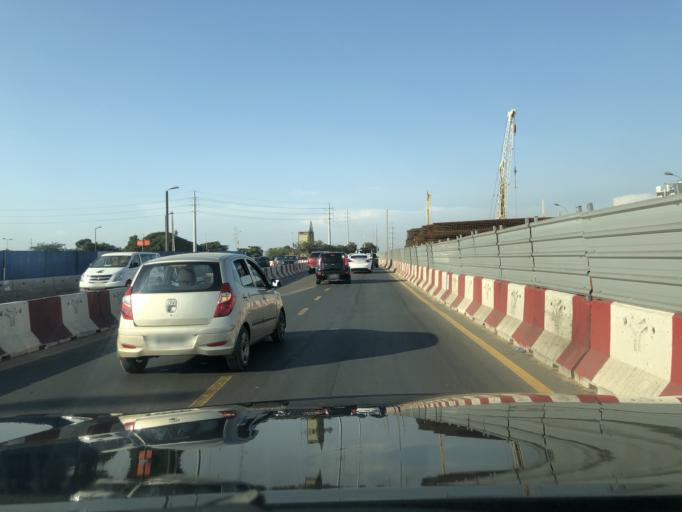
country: AO
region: Luanda
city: Luanda
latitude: -8.9093
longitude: 13.1795
